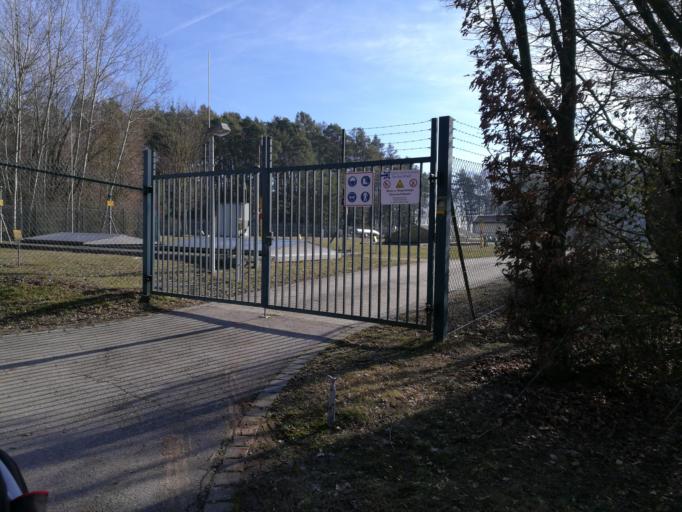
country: DE
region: Bavaria
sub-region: Regierungsbezirk Mittelfranken
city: Obermichelbach
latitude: 49.5352
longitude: 10.8909
